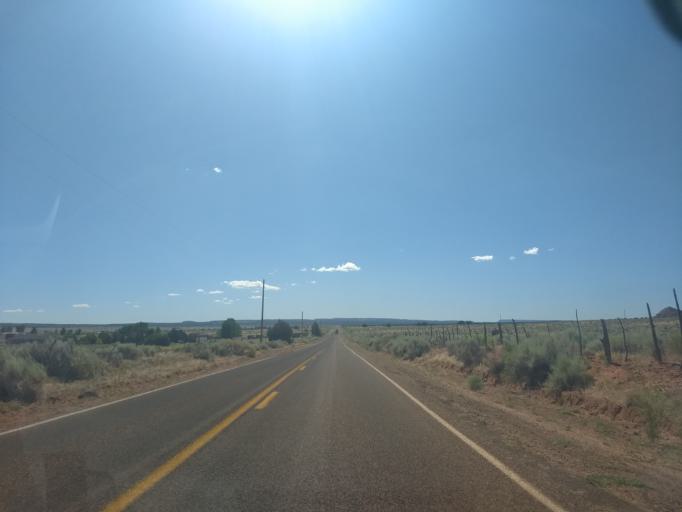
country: US
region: Arizona
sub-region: Mohave County
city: Colorado City
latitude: 36.9469
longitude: -112.9245
